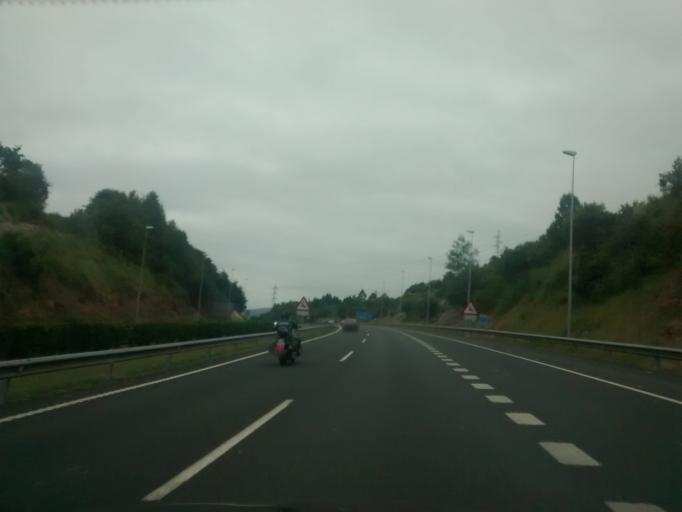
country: ES
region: Cantabria
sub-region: Provincia de Cantabria
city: Reocin
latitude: 43.3534
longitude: -4.0872
